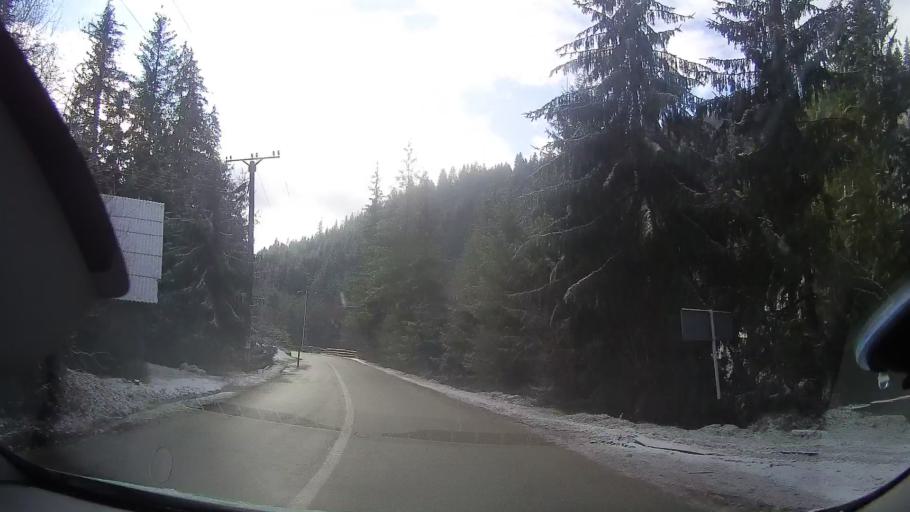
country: RO
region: Alba
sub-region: Comuna Horea
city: Horea
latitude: 46.4875
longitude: 22.9604
